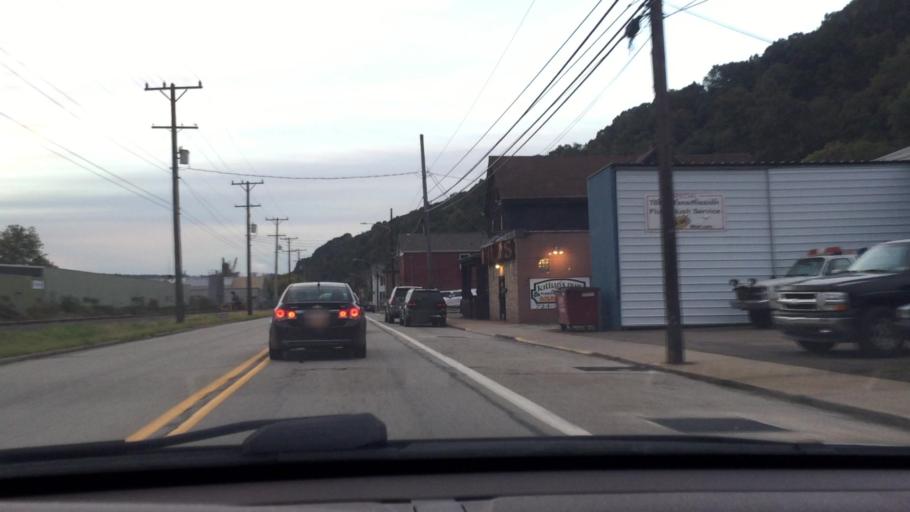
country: US
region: Pennsylvania
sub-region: Westmoreland County
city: Arnold
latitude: 40.5762
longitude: -79.7782
